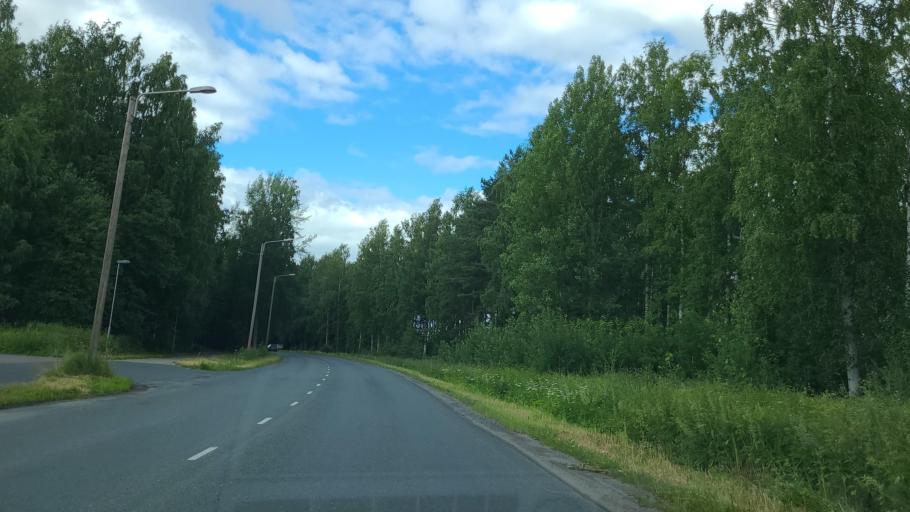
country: FI
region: Northern Savo
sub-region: Kuopio
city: Kuopio
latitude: 62.9343
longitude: 27.6661
